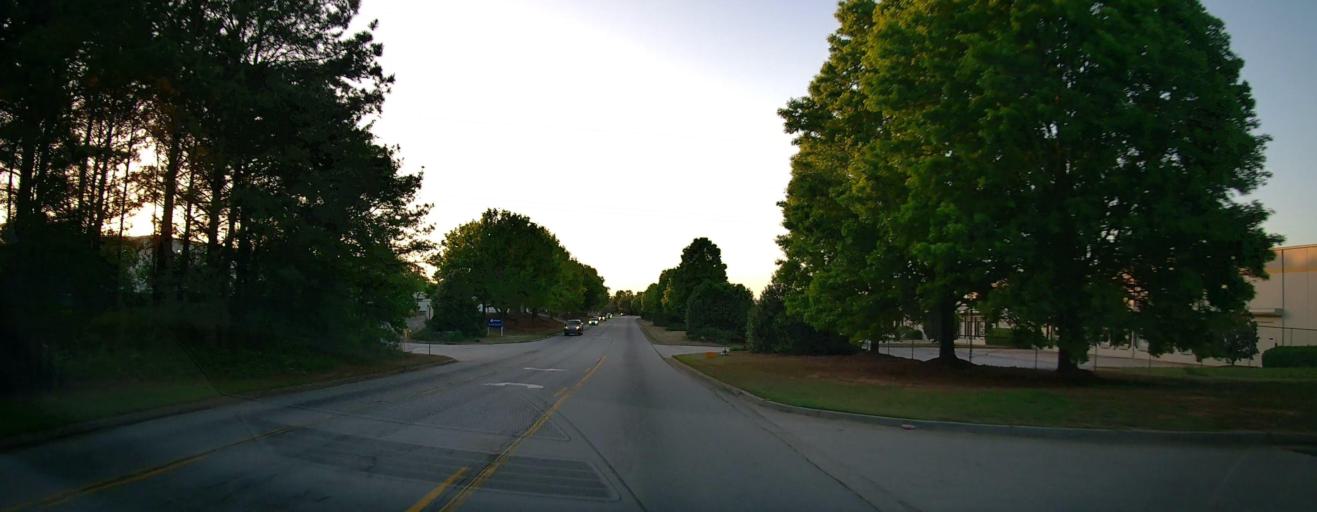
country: US
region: Georgia
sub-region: Henry County
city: McDonough
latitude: 33.4089
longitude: -84.1507
